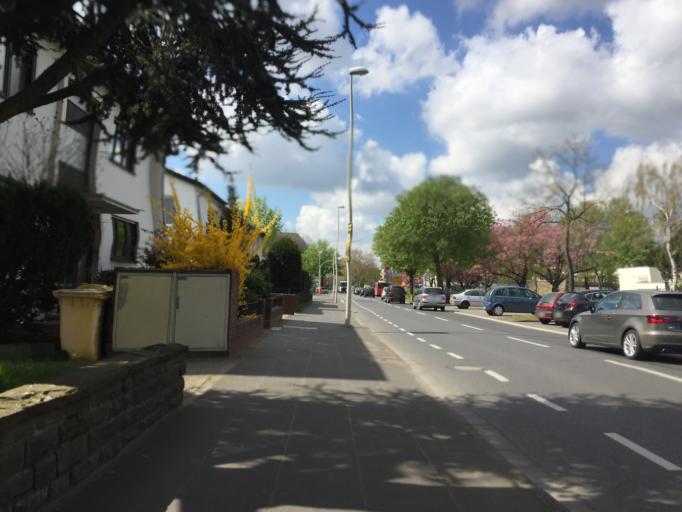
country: DE
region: North Rhine-Westphalia
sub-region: Regierungsbezirk Koln
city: Bonn
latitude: 50.7518
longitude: 7.0791
